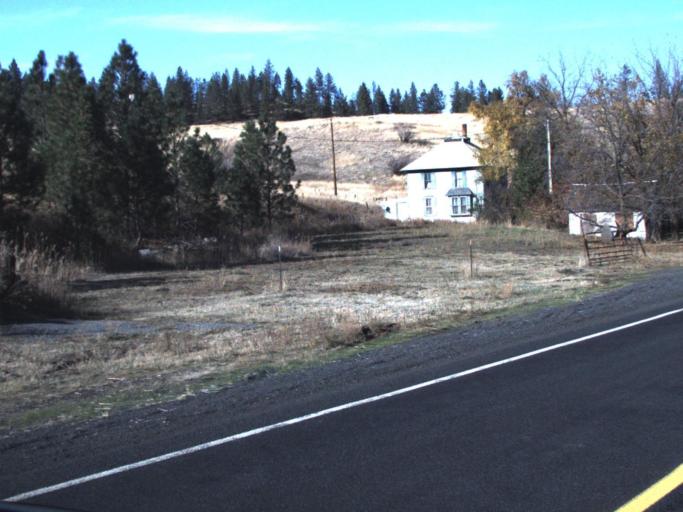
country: US
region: Washington
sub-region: Lincoln County
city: Davenport
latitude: 47.8829
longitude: -118.2645
